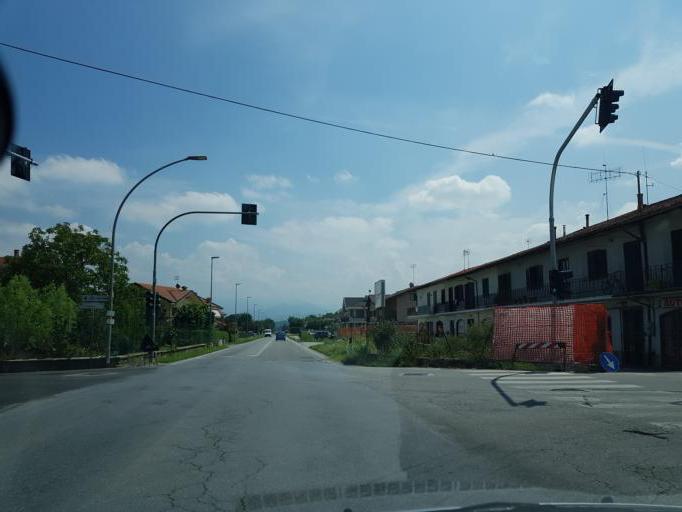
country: IT
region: Piedmont
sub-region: Provincia di Cuneo
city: Caraglio
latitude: 44.4144
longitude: 7.4368
